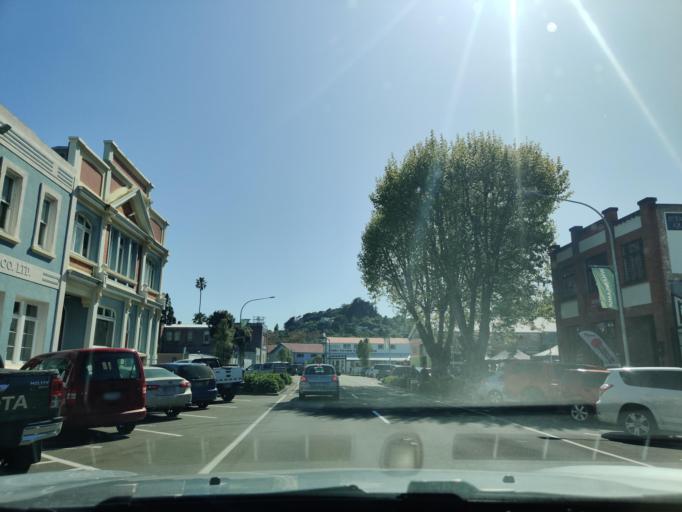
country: NZ
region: Manawatu-Wanganui
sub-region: Wanganui District
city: Wanganui
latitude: -39.9336
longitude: 175.0566
